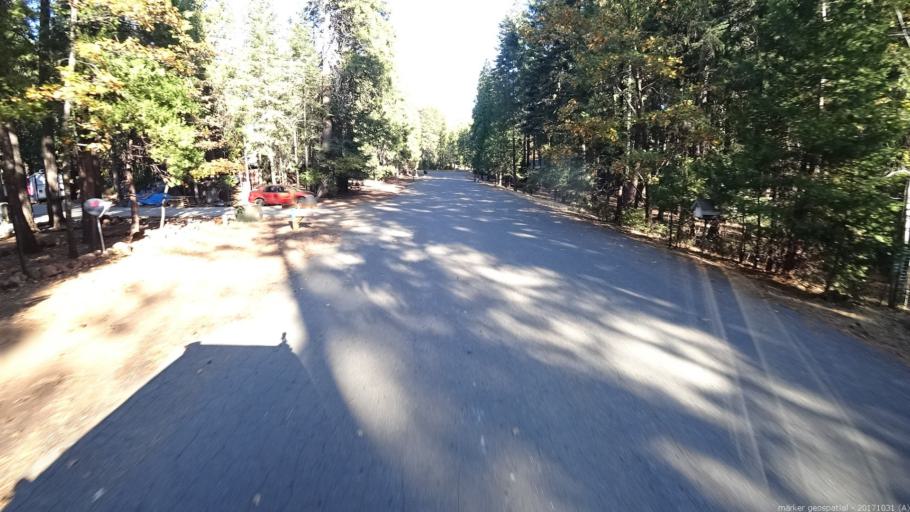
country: US
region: California
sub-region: Shasta County
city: Shingletown
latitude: 40.5033
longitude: -121.8999
